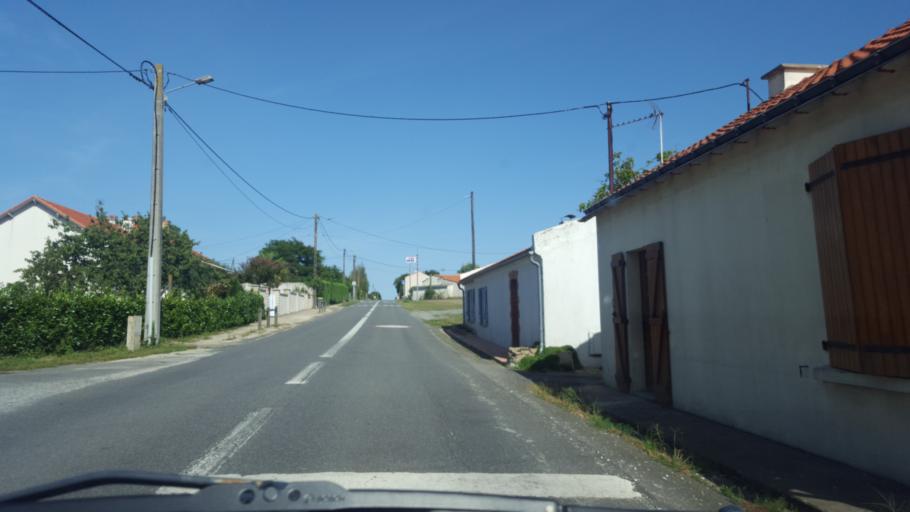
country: FR
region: Pays de la Loire
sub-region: Departement de la Loire-Atlantique
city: La Limouziniere
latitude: 46.9891
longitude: -1.6141
